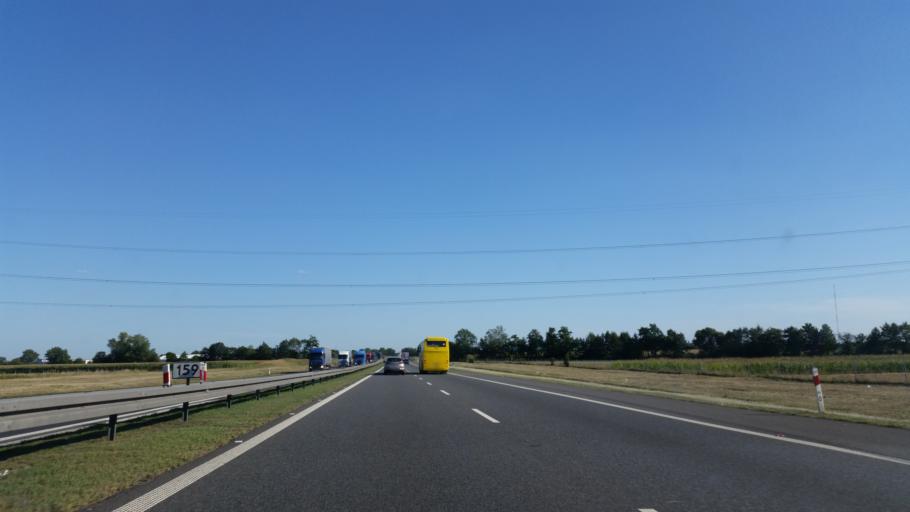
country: PL
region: Lower Silesian Voivodeship
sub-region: Powiat wroclawski
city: Zorawina
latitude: 51.0137
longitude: 17.0259
